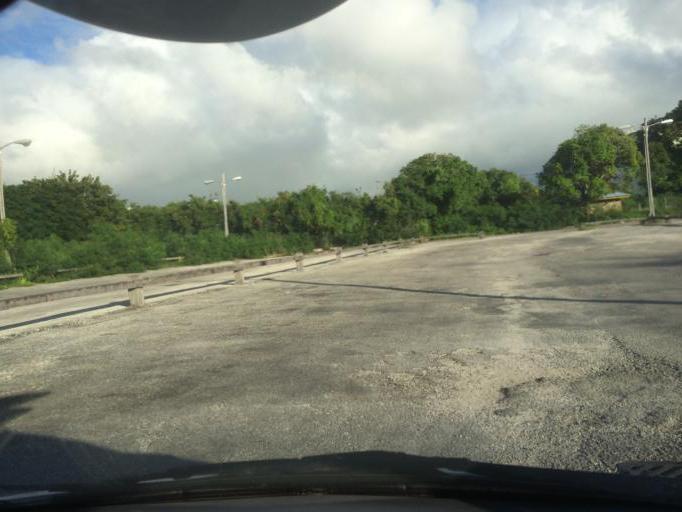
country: BB
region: Christ Church
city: Oistins
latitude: 13.0644
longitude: -59.5422
